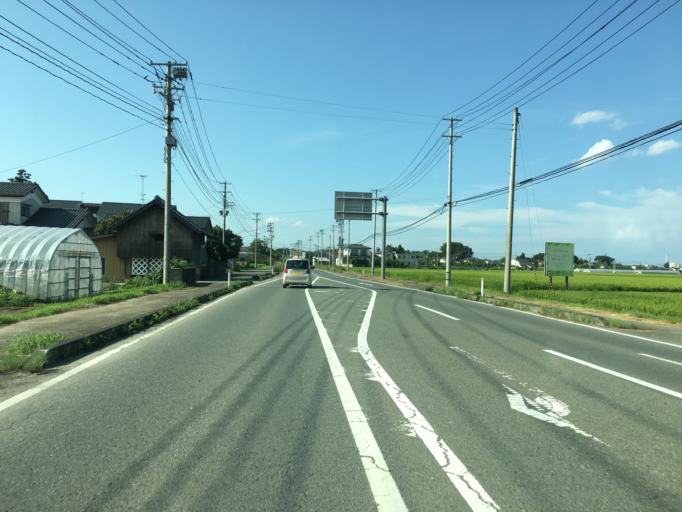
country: JP
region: Miyagi
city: Marumori
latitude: 37.7859
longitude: 140.9139
